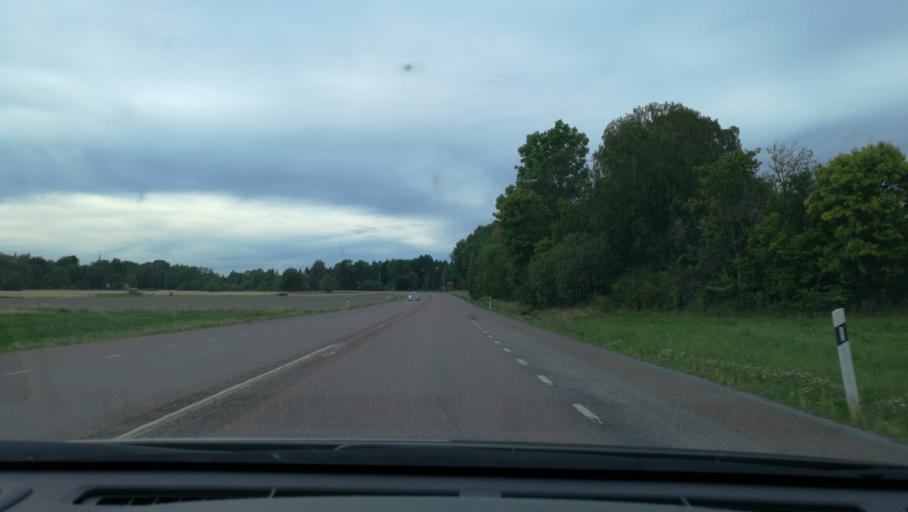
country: SE
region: Vaestmanland
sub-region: Kungsors Kommun
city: Kungsoer
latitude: 59.4439
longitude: 16.0452
